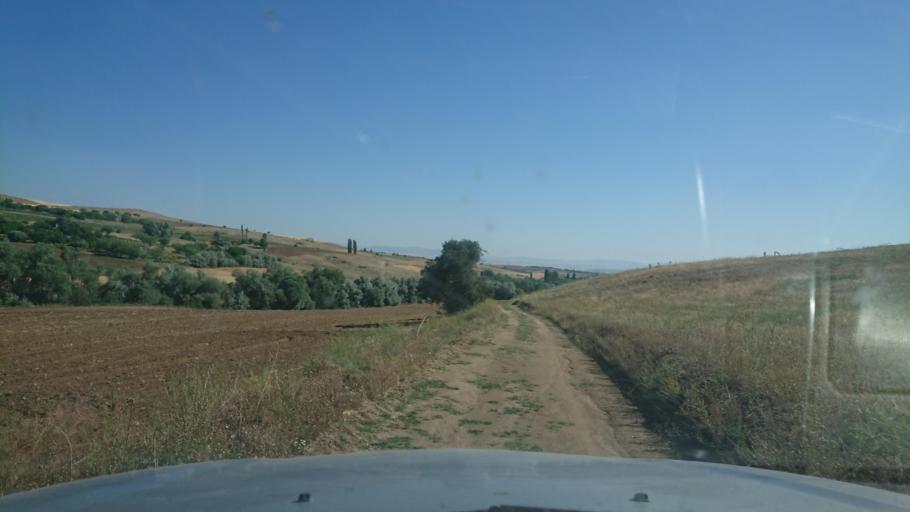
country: TR
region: Aksaray
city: Agacoren
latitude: 38.8422
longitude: 33.9258
